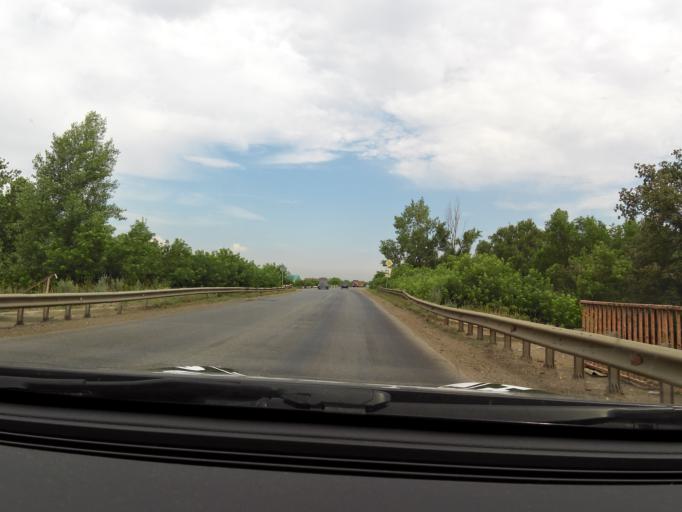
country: RU
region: Bashkortostan
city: Iglino
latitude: 54.7750
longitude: 56.2560
